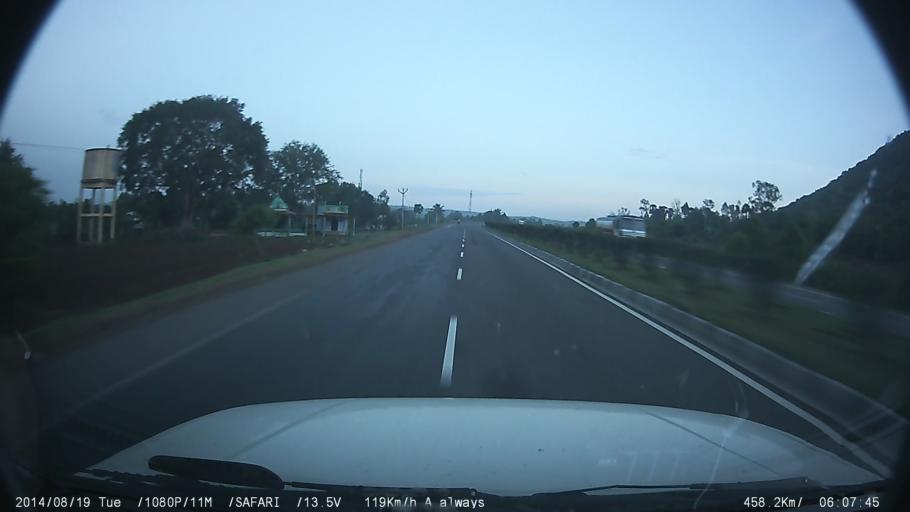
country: IN
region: Tamil Nadu
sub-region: Salem
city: Omalur
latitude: 11.9050
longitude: 78.0606
